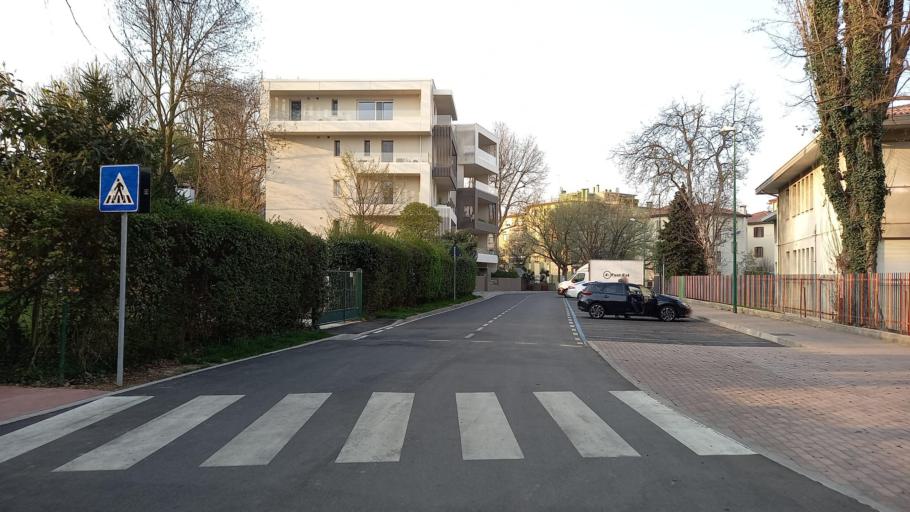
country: IT
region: Veneto
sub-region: Provincia di Venezia
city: Mestre
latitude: 45.4898
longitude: 12.2275
